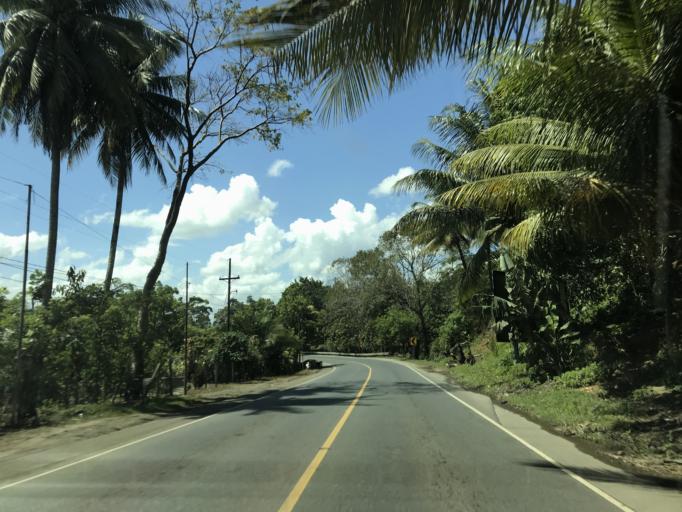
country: GT
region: Izabal
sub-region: Municipio de Puerto Barrios
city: Puerto Barrios
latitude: 15.6564
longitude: -88.5510
